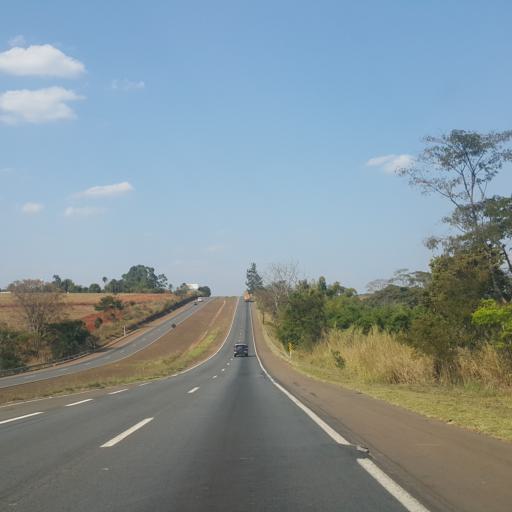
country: BR
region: Goias
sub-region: Abadiania
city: Abadiania
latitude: -16.2774
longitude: -48.7861
